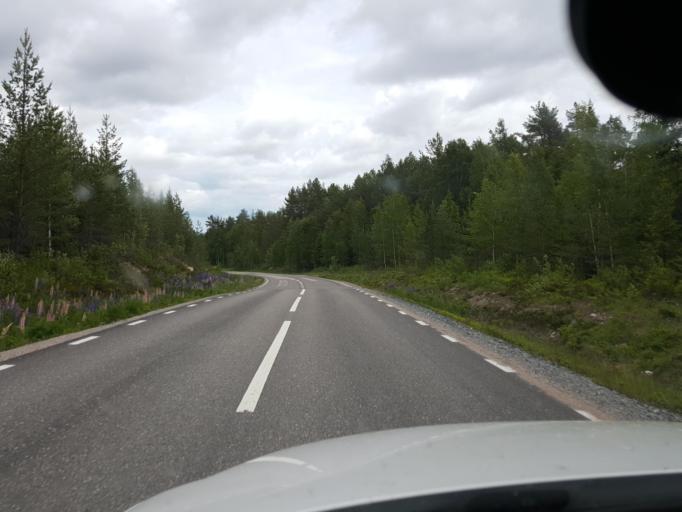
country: SE
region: Gaevleborg
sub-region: Ljusdals Kommun
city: Farila
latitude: 61.7761
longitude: 15.5898
